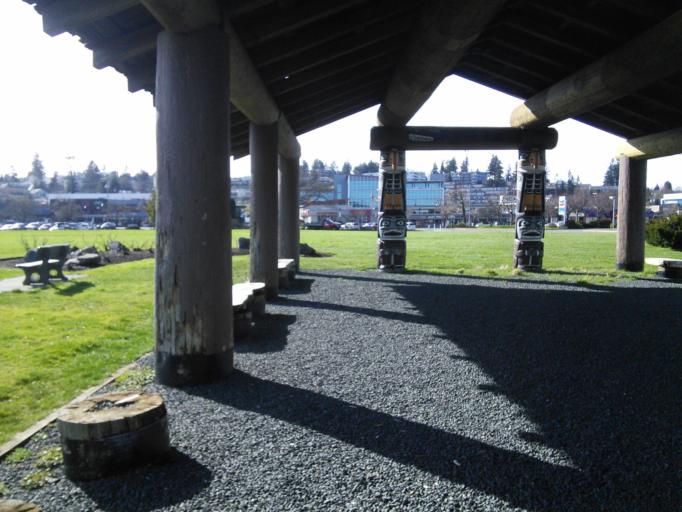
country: CA
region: British Columbia
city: Campbell River
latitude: 50.0263
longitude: -125.2405
